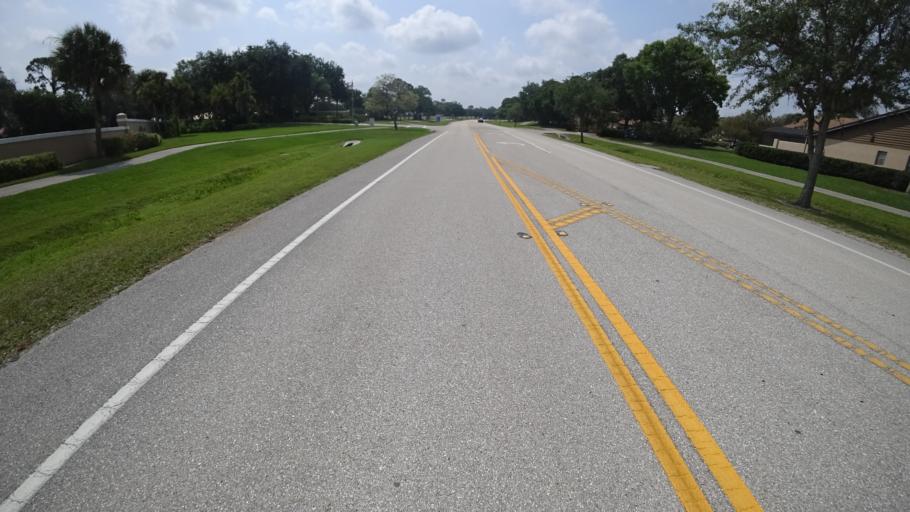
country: US
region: Florida
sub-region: Sarasota County
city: Desoto Lakes
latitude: 27.4102
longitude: -82.4885
